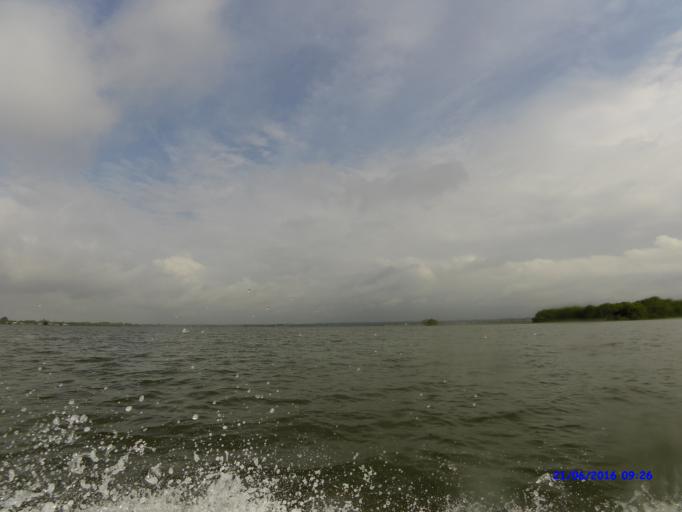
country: BJ
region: Mono
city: Come
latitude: 6.4227
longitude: 1.9378
